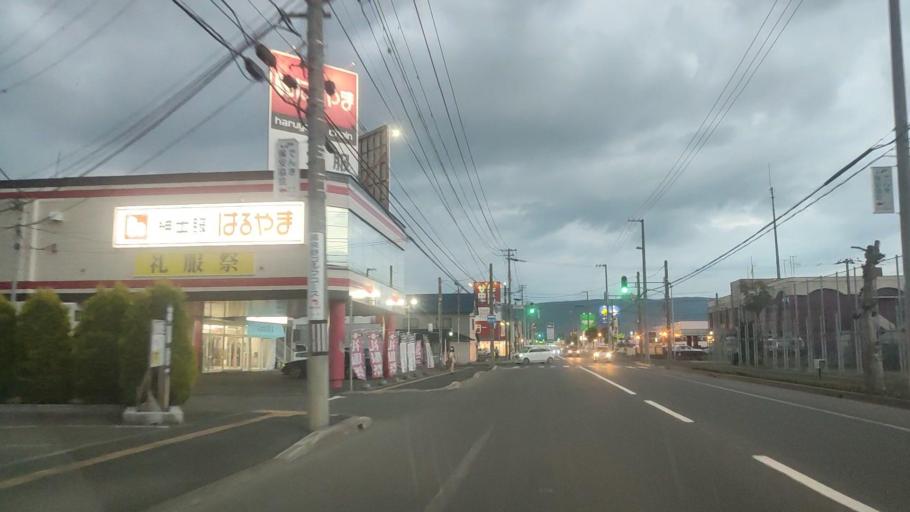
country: JP
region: Hokkaido
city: Shimo-furano
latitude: 43.3401
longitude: 142.3907
